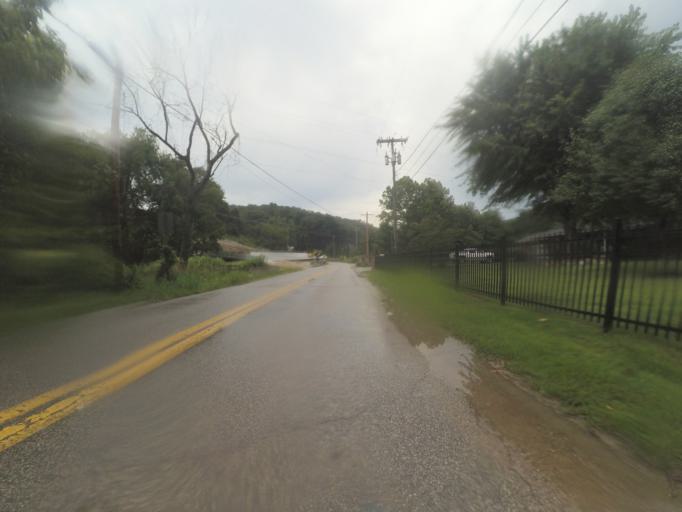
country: US
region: West Virginia
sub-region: Cabell County
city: Huntington
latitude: 38.3868
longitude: -82.3927
